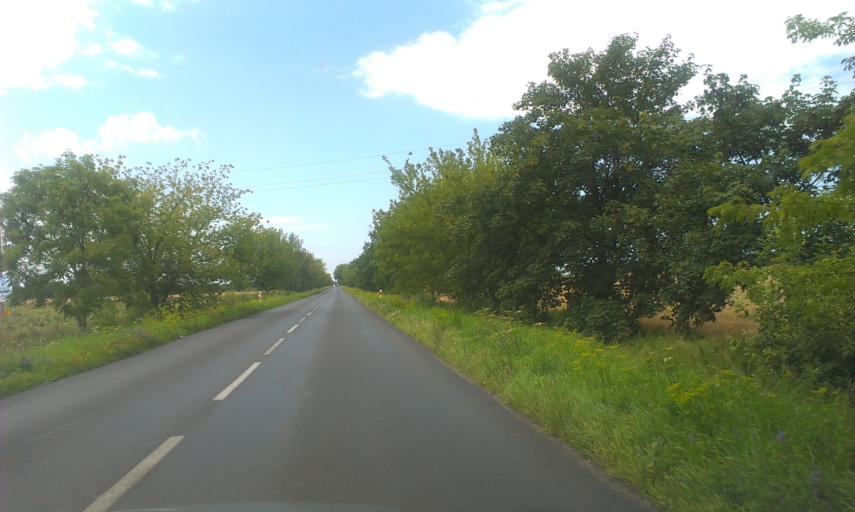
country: PL
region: West Pomeranian Voivodeship
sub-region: Powiat kolobrzeski
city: Dygowo
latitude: 54.1430
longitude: 15.6907
